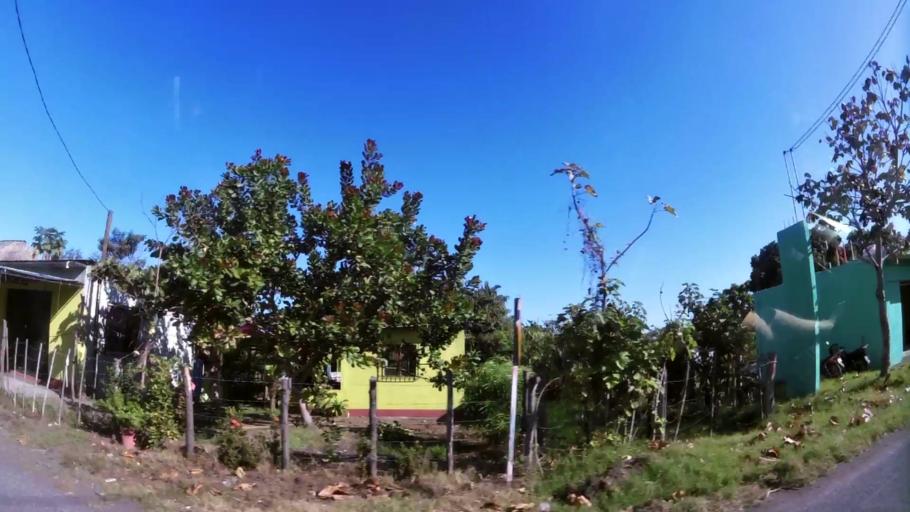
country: GT
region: Santa Rosa
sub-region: Municipio de Taxisco
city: Taxisco
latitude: 13.8961
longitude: -90.4864
